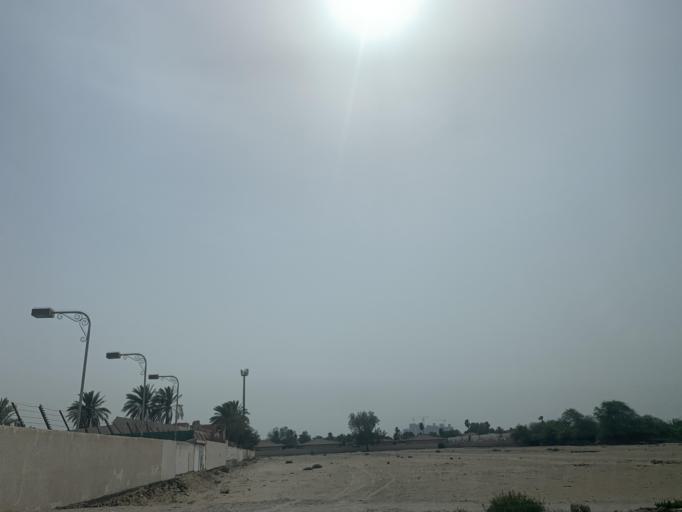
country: BH
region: Manama
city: Jidd Hafs
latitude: 26.2010
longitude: 50.4780
